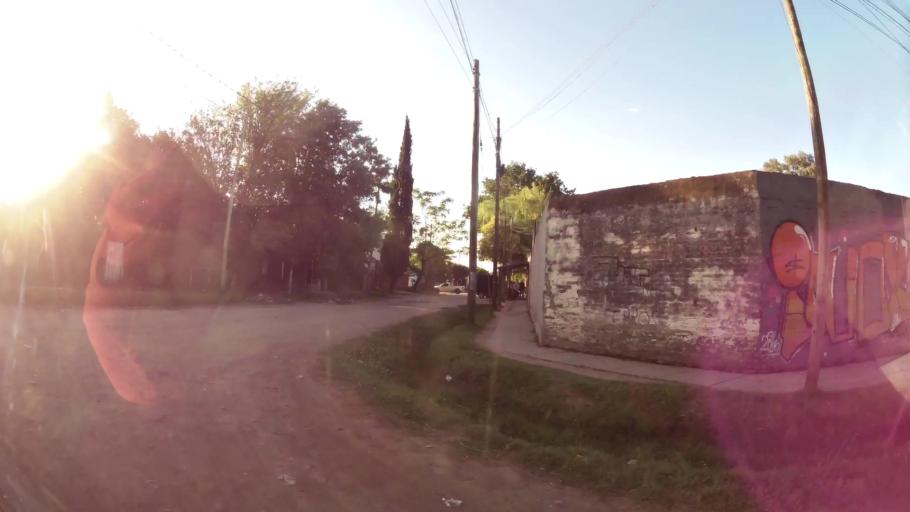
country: AR
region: Buenos Aires
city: Santa Catalina - Dique Lujan
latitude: -34.4711
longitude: -58.7494
